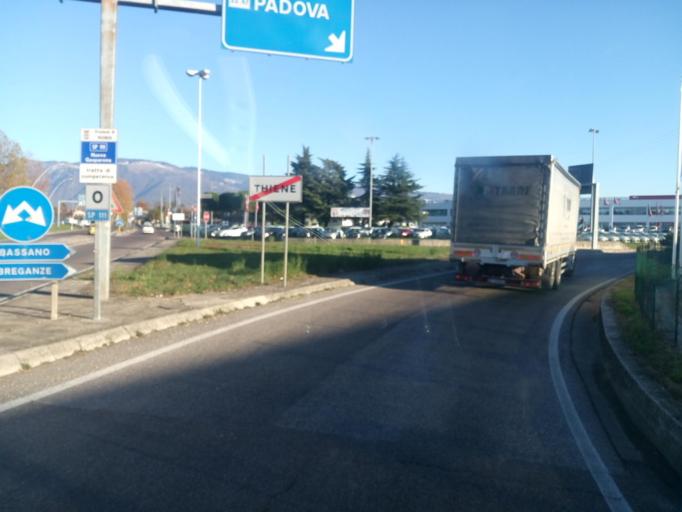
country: IT
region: Veneto
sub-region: Provincia di Vicenza
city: Thiene
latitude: 45.6917
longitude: 11.4831
